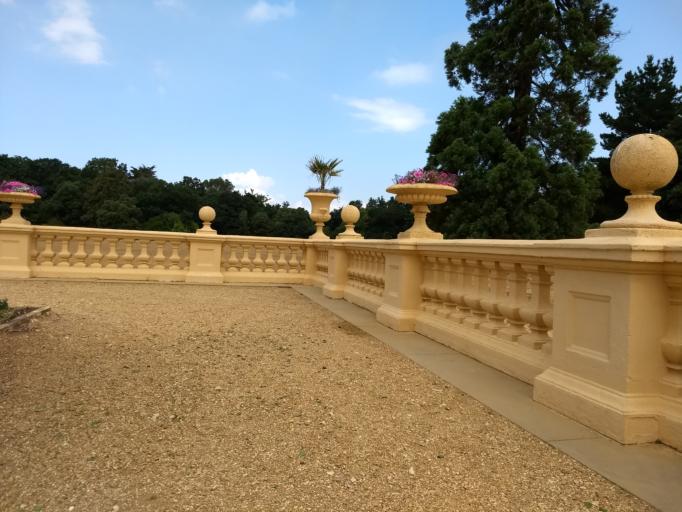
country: GB
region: England
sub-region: Isle of Wight
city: East Cowes
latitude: 50.7514
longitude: -1.2692
